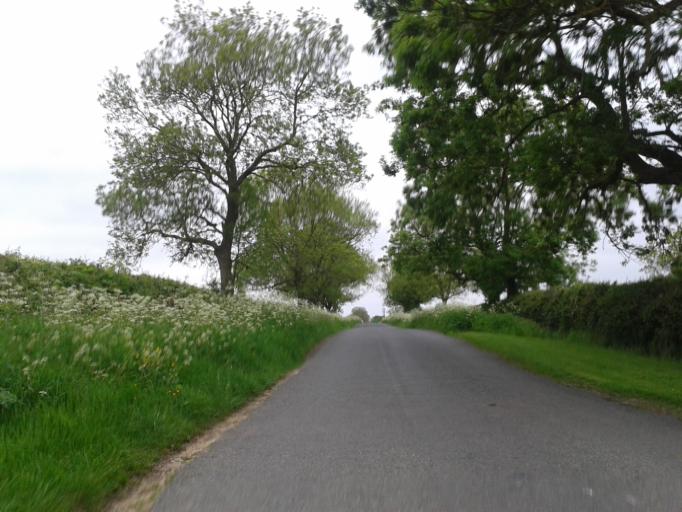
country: GB
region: England
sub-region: Leicestershire
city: Wigston Magna
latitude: 52.5261
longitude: -1.0774
